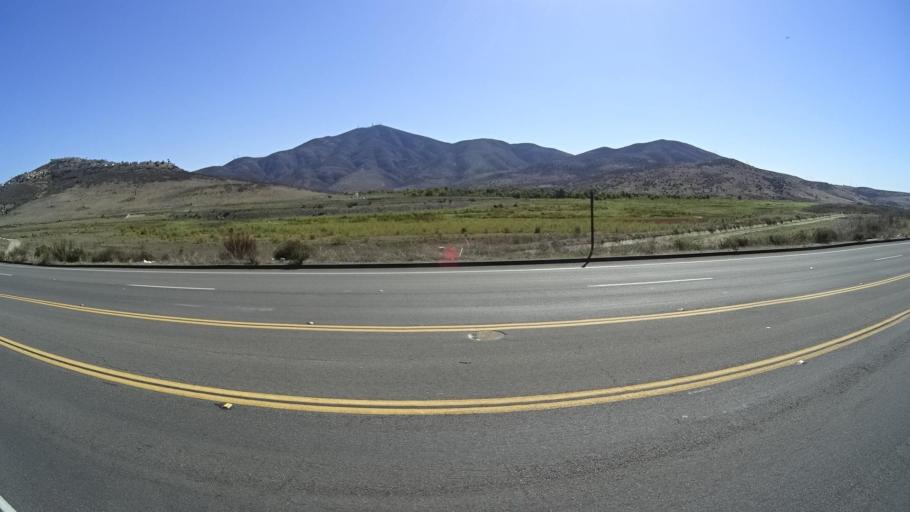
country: US
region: California
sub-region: San Diego County
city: La Presa
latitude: 32.7125
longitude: -116.9813
